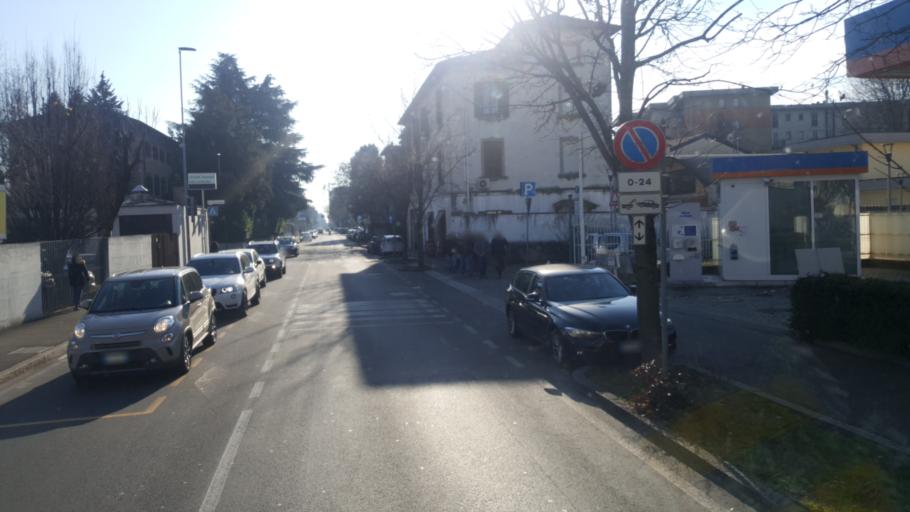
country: IT
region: Lombardy
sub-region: Provincia di Bergamo
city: Bergamo
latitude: 45.6822
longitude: 9.6620
